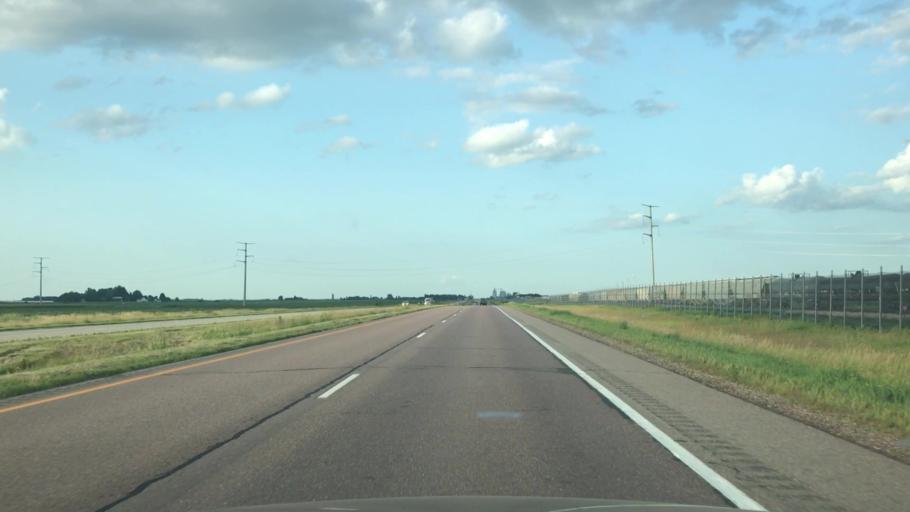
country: US
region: Minnesota
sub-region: Nobles County
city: Worthington
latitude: 43.6690
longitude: -95.5170
